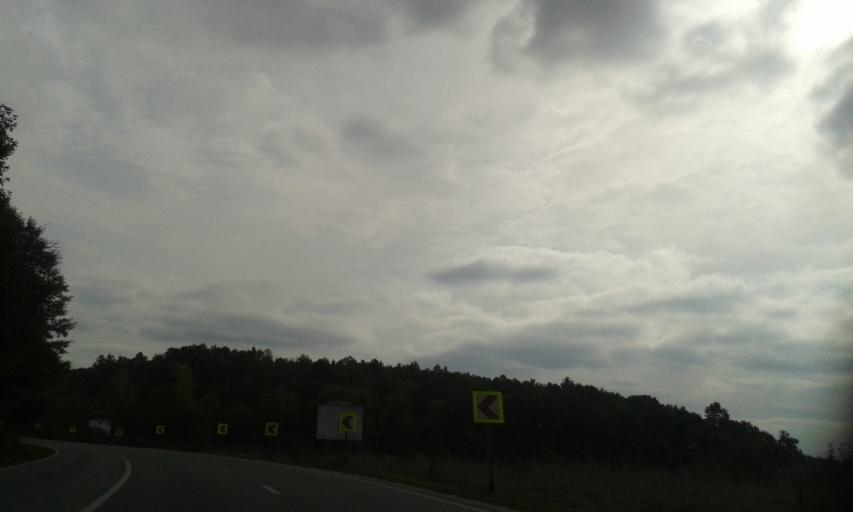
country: RO
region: Gorj
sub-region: Comuna Balanesti
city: Balanesti
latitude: 45.0338
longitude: 23.3761
